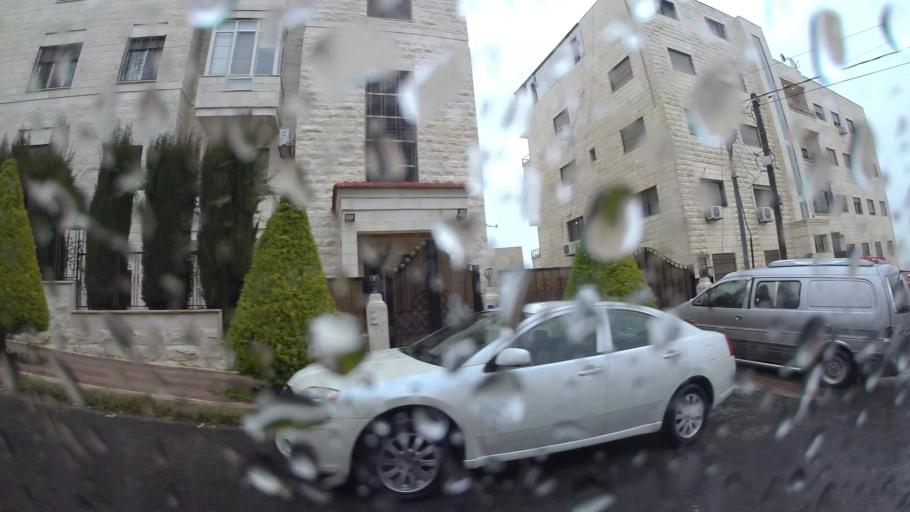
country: JO
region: Amman
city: Al Jubayhah
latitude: 32.0255
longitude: 35.8907
